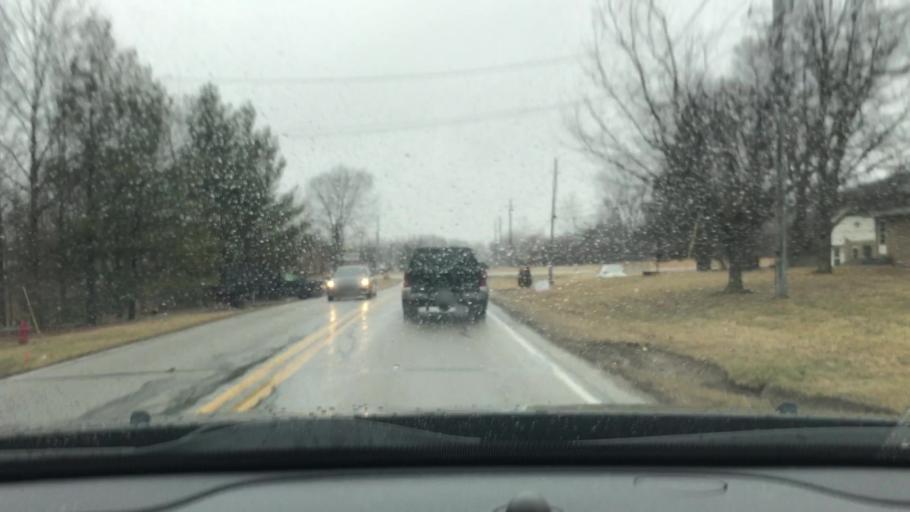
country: US
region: Indiana
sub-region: Morgan County
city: Mooresville
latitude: 39.5879
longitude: -86.3317
